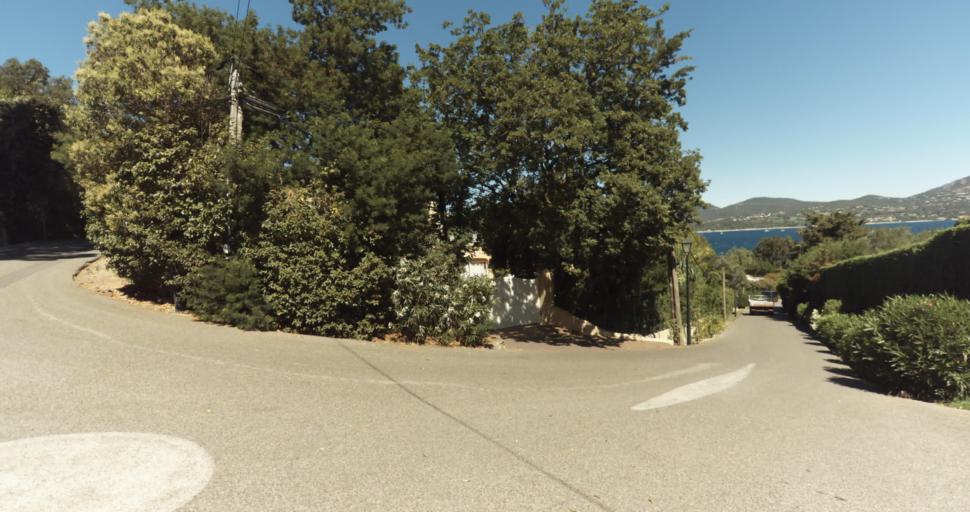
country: FR
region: Provence-Alpes-Cote d'Azur
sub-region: Departement du Var
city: Gassin
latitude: 43.2611
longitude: 6.6026
